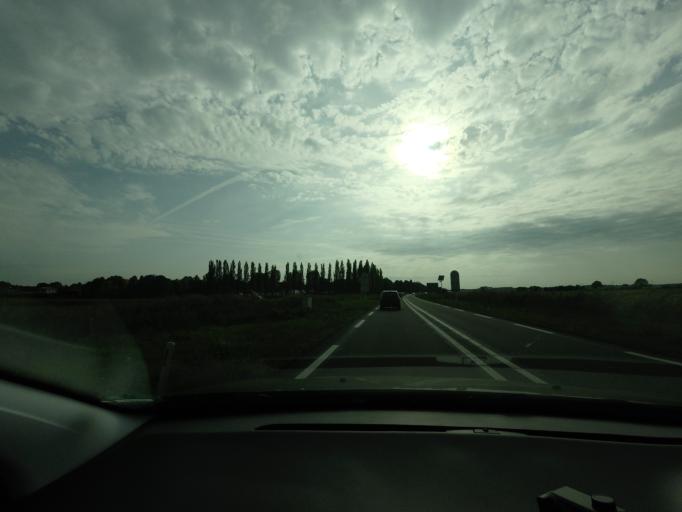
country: NL
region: North Brabant
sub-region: Gemeente Made en Drimmelen
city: Made
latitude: 51.6532
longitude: 4.7591
